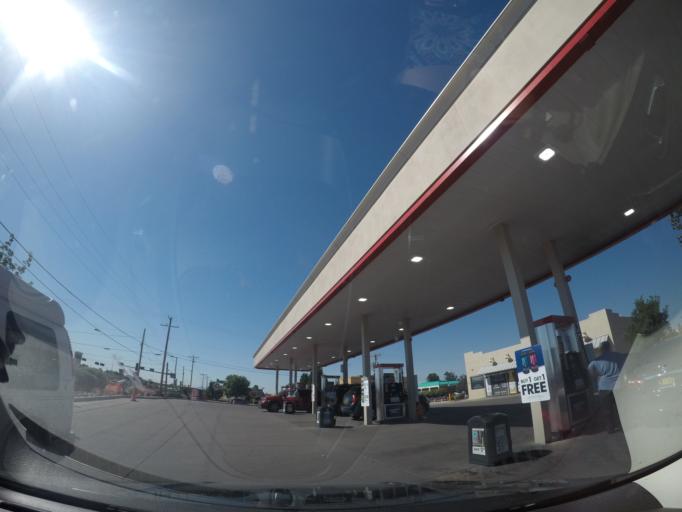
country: US
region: New Mexico
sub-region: Dona Ana County
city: Las Cruces
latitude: 32.2939
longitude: -106.7865
